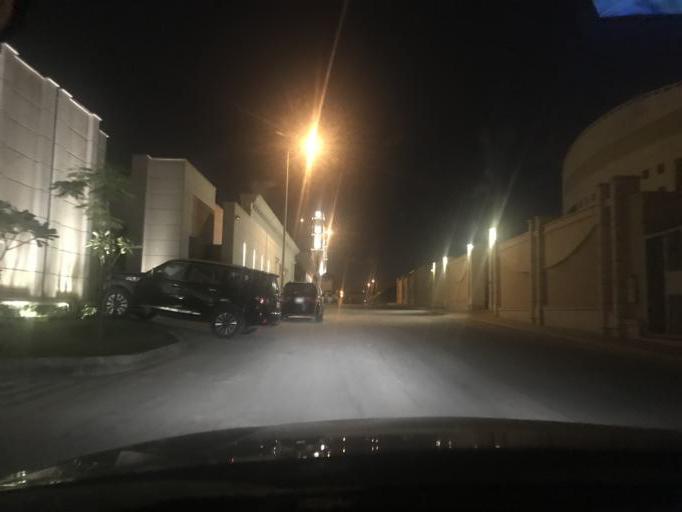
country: SA
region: Ar Riyad
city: Riyadh
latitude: 24.7263
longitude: 46.7521
